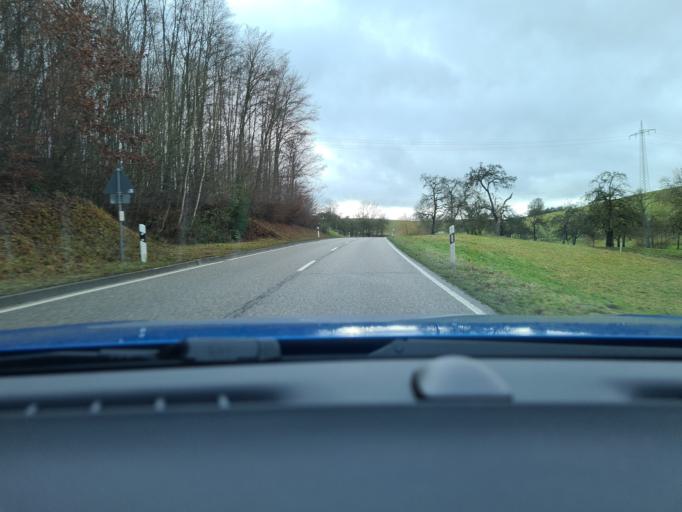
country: DE
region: Baden-Wuerttemberg
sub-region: Karlsruhe Region
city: Mauer
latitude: 49.3291
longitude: 8.7902
